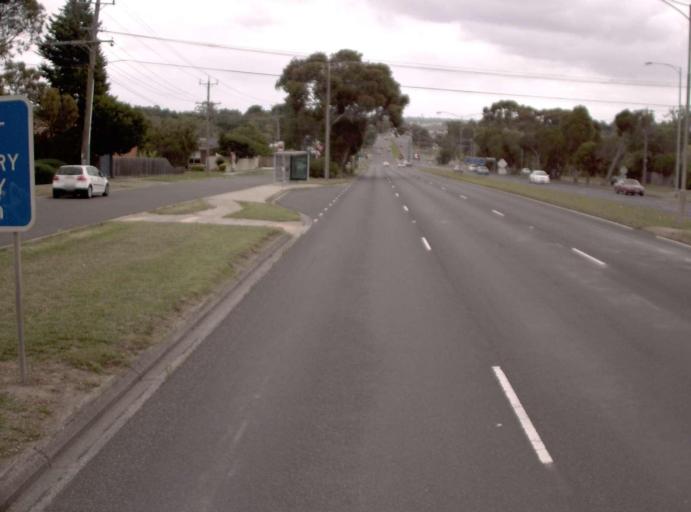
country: AU
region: Victoria
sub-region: Maroondah
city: Croydon Hills
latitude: -37.7937
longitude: 145.2600
